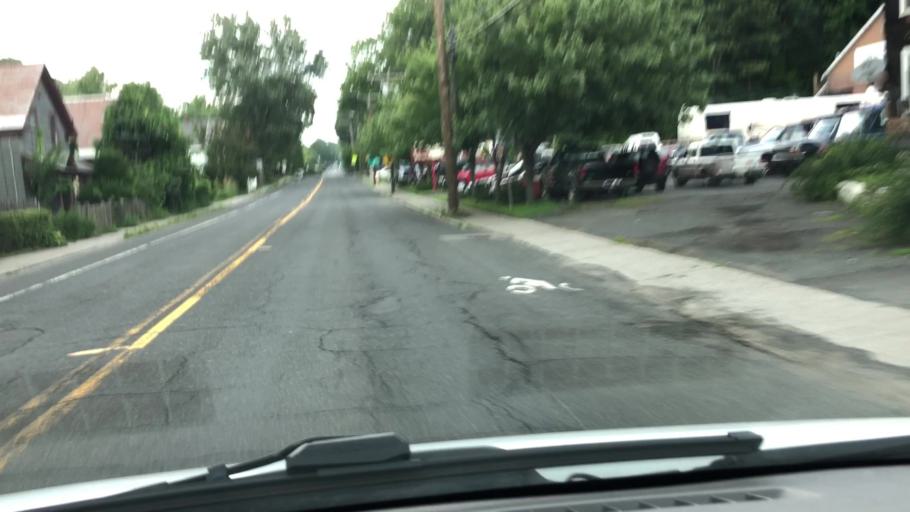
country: US
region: Massachusetts
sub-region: Franklin County
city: Greenfield
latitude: 42.5764
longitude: -72.5977
